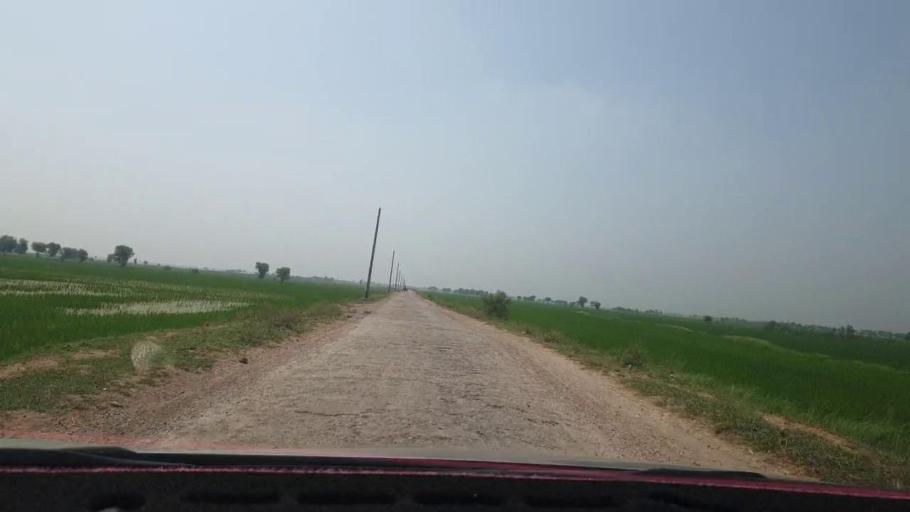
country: PK
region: Sindh
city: Warah
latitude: 27.4144
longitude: 67.8445
